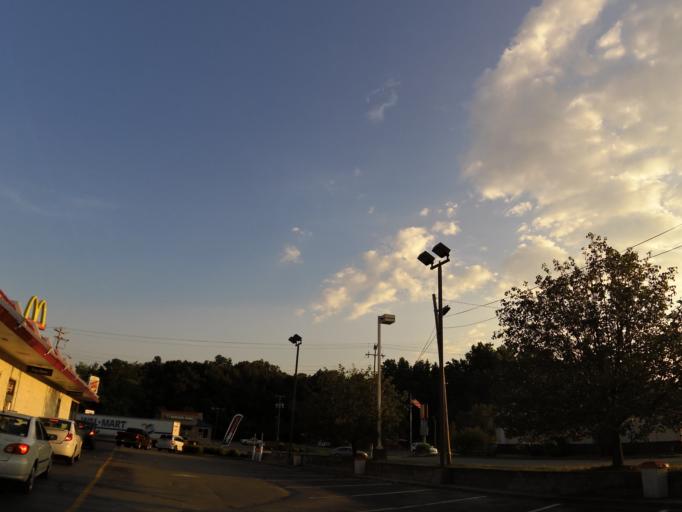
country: US
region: Tennessee
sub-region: Henry County
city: Paris
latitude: 36.2902
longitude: -88.3137
